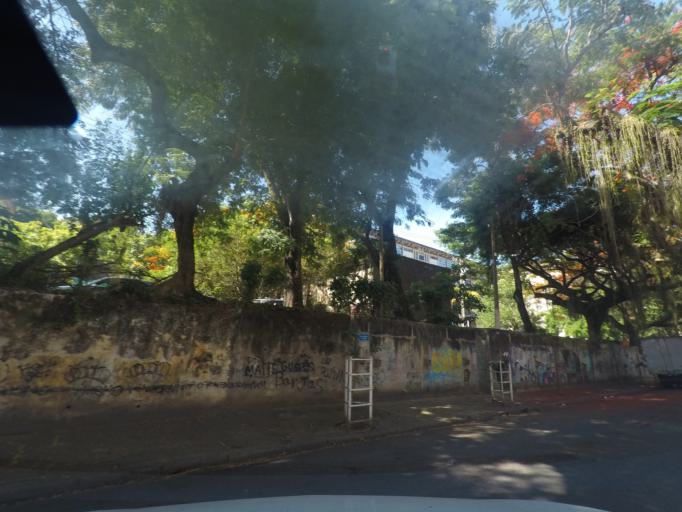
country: BR
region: Rio de Janeiro
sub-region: Niteroi
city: Niteroi
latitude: -22.9058
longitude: -43.1323
